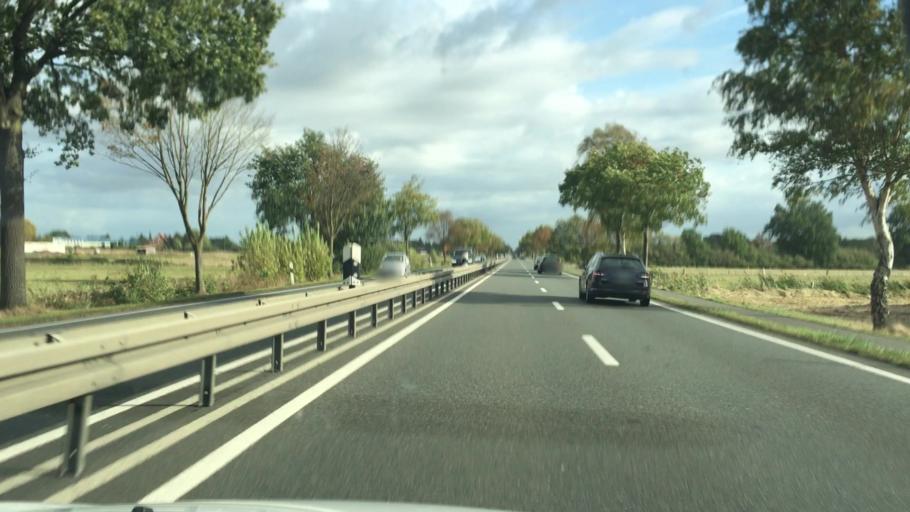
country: DE
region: Lower Saxony
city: Garbsen
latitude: 52.4511
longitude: 9.5594
